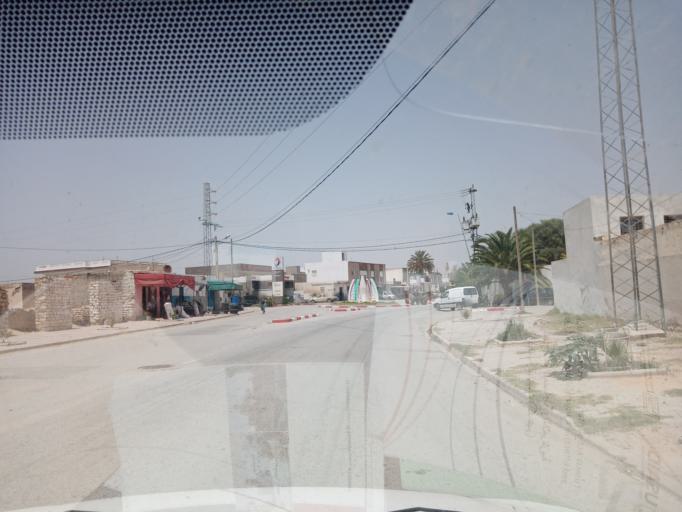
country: TN
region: Al Qayrawan
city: Sbikha
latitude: 36.1150
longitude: 10.0971
